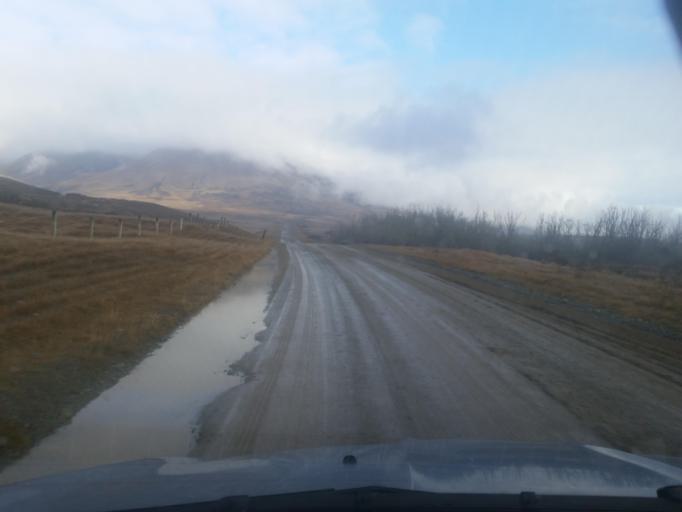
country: NZ
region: Canterbury
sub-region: Ashburton District
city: Methven
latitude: -43.6156
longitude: 171.0935
